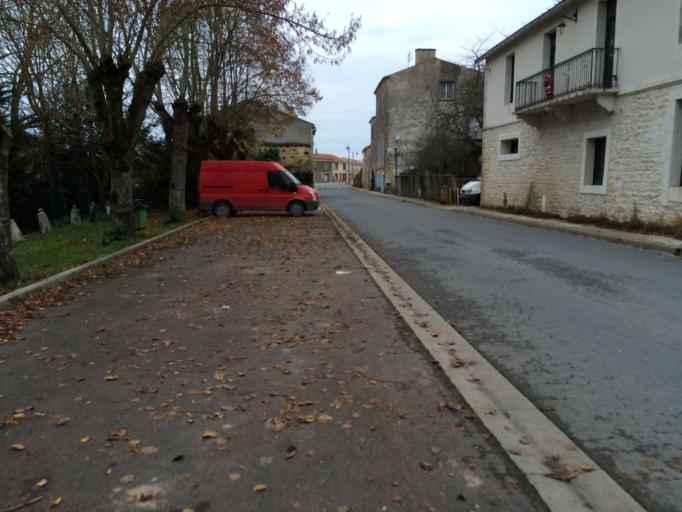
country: FR
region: Pays de la Loire
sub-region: Departement de la Vendee
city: Chaille-les-Marais
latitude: 46.3929
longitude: -1.0217
